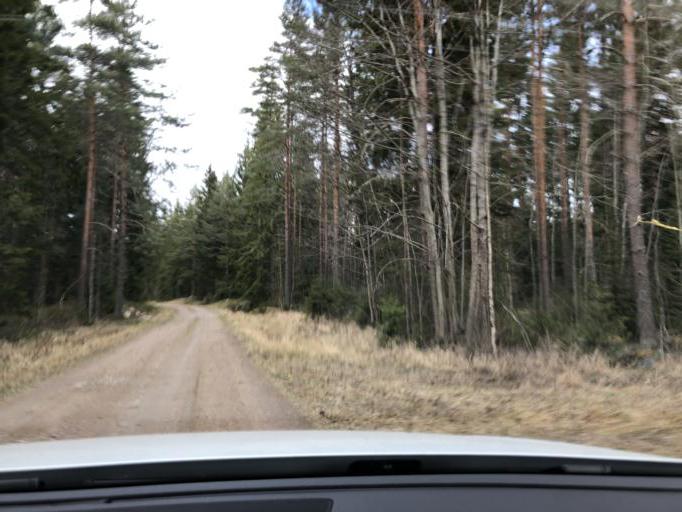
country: SE
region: Gaevleborg
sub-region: Gavle Kommun
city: Hedesunda
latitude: 60.3410
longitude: 17.1050
